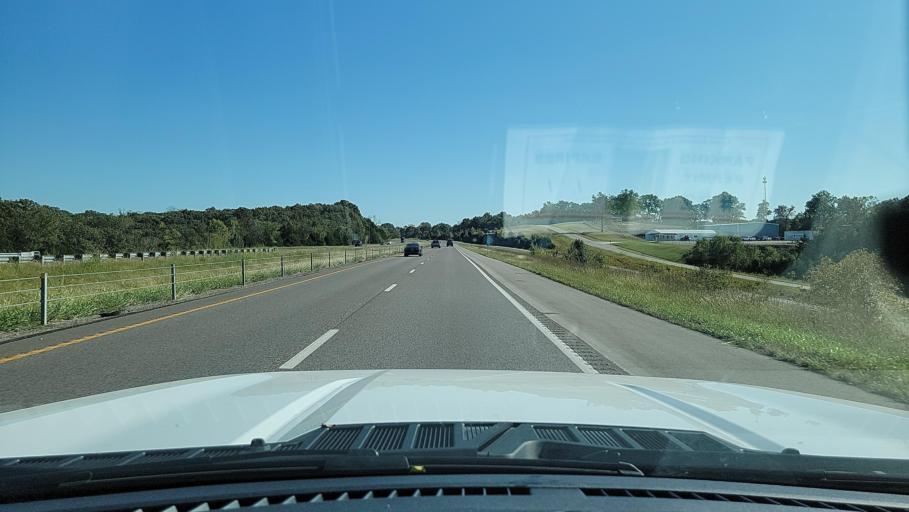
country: US
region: Missouri
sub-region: Sainte Genevieve County
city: Sainte Genevieve
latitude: 37.9740
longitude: -90.1902
